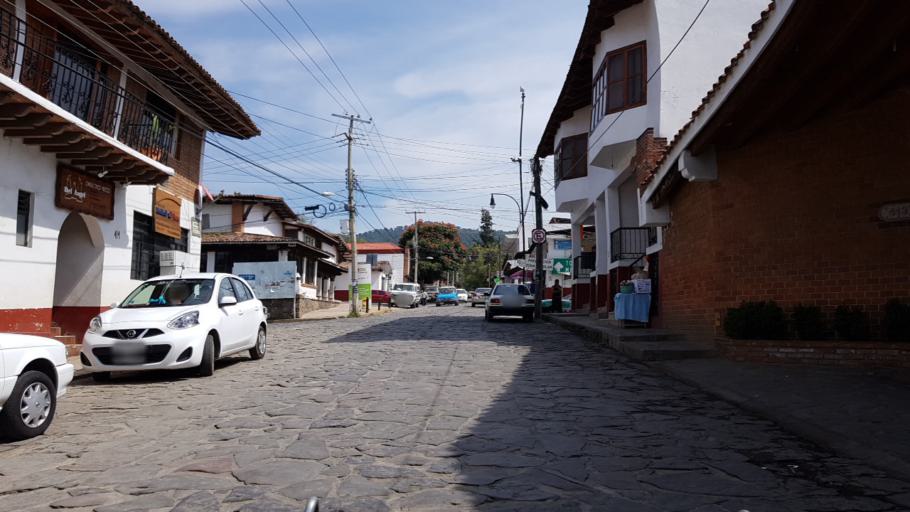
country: MX
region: Mexico
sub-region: Valle de Bravo
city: Colonia Rincon Villa del Valle
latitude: 19.2024
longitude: -100.1263
